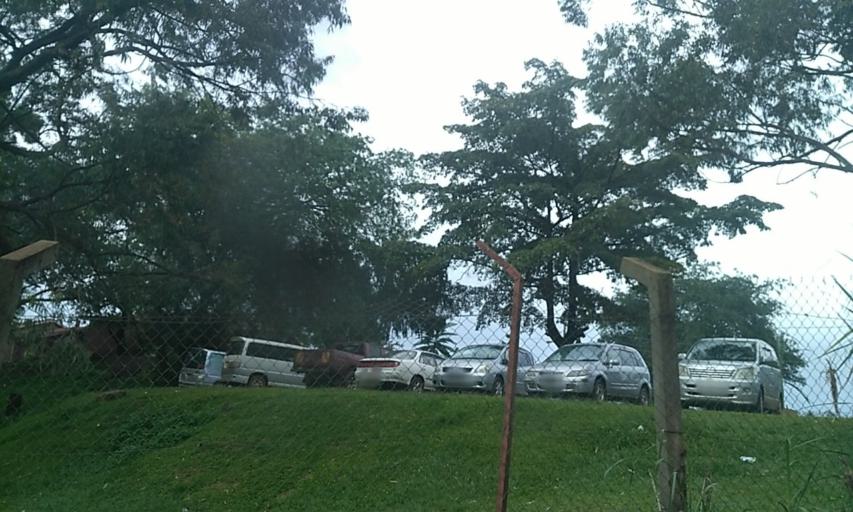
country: UG
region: Central Region
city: Kampala Central Division
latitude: 0.3351
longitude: 32.5864
